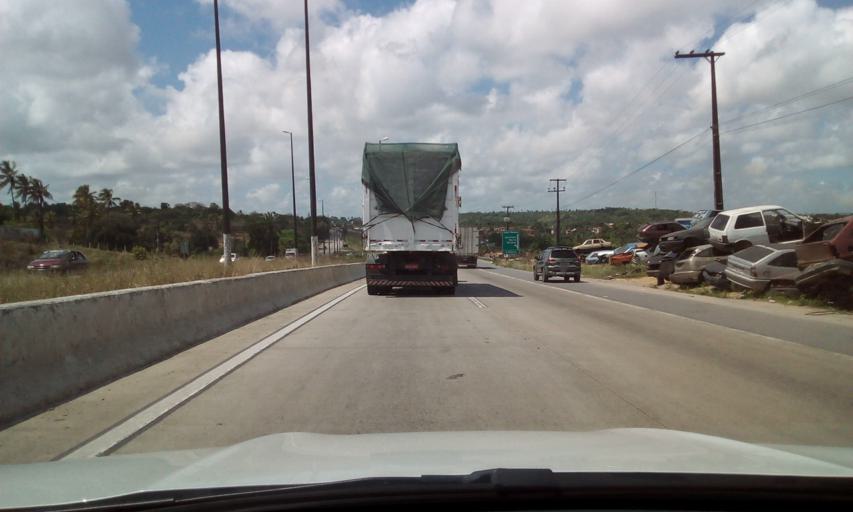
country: BR
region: Pernambuco
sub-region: Igarassu
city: Igarassu
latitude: -7.8192
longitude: -34.9170
